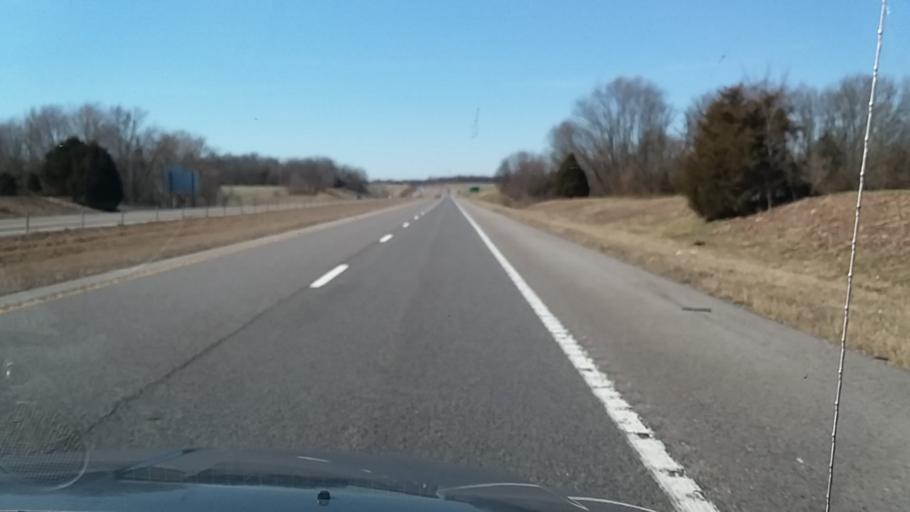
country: US
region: Missouri
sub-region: Perry County
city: Perryville
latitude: 37.5870
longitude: -89.7684
